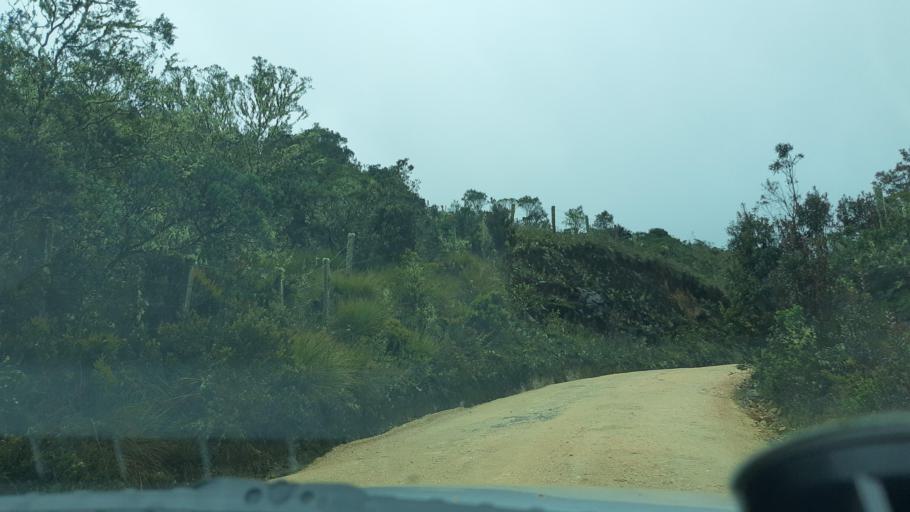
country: CO
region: Cundinamarca
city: Villapinzon
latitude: 5.2064
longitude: -73.5526
